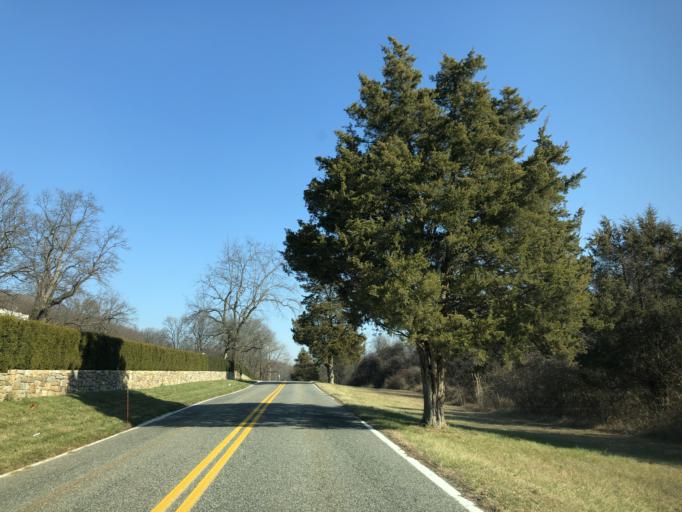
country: US
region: Pennsylvania
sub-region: Chester County
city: Chesterbrook
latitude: 40.0828
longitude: -75.4663
